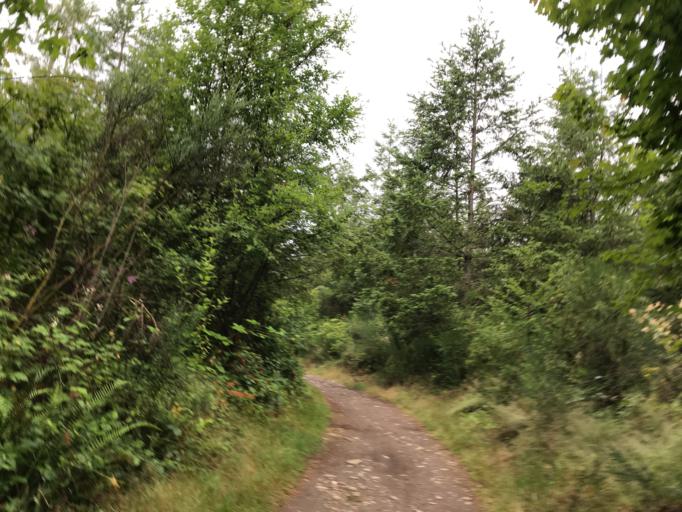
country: US
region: Washington
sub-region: King County
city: Black Diamond
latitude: 47.3364
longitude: -122.0110
